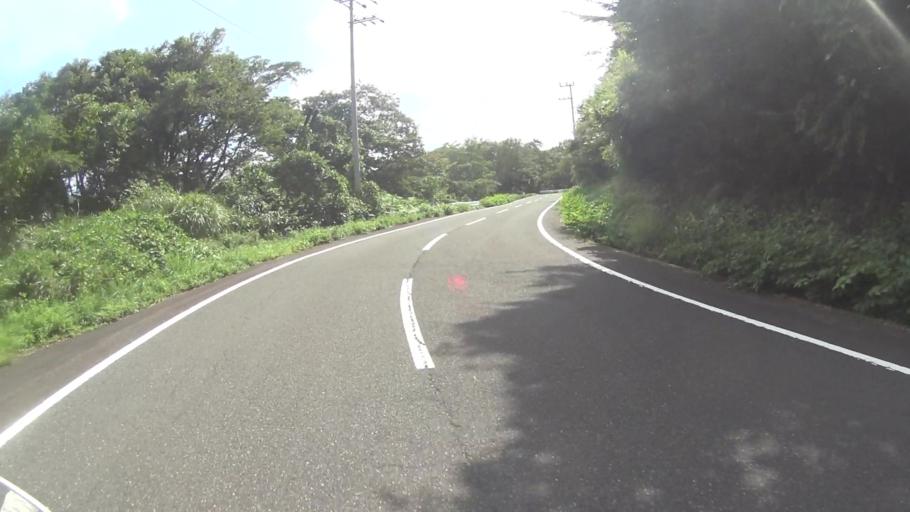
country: JP
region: Kyoto
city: Miyazu
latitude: 35.7243
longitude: 135.1880
